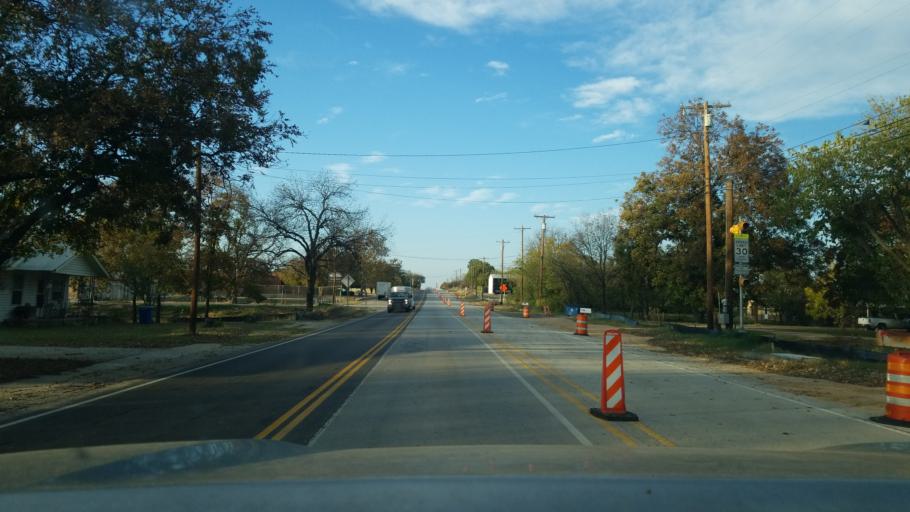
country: US
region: Texas
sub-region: Brown County
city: Lake Brownwood
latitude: 32.1036
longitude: -98.9643
